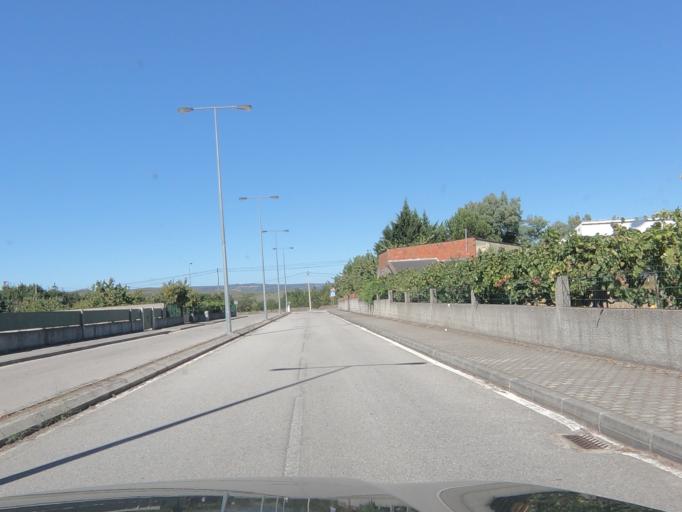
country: PT
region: Vila Real
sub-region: Valpacos
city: Valpacos
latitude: 41.6611
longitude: -7.3167
